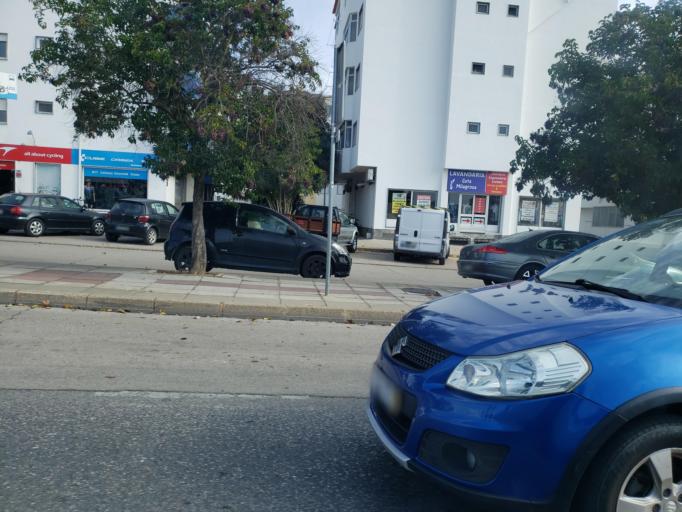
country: PT
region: Faro
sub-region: Portimao
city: Portimao
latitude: 37.1446
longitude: -8.5488
